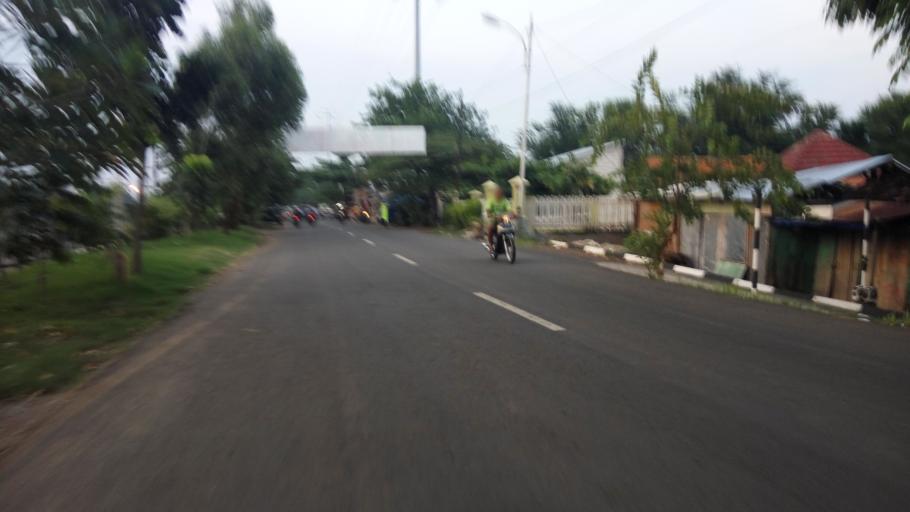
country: ID
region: Central Java
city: Semarang
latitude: -6.9861
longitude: 110.4028
